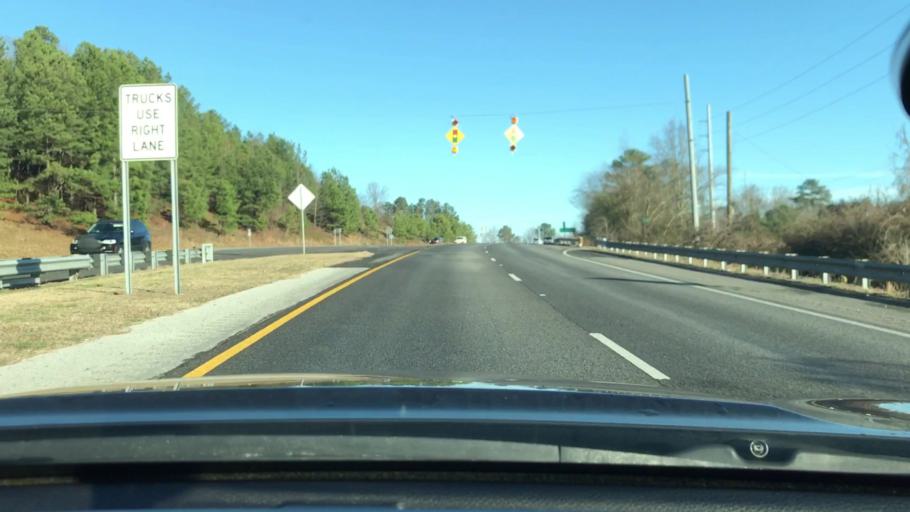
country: US
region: Alabama
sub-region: Shelby County
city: Meadowbrook
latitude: 33.3854
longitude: -86.6683
